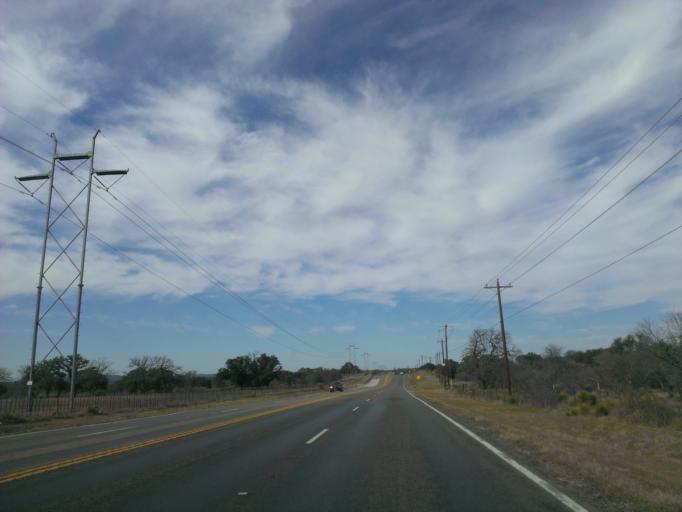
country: US
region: Texas
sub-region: Burnet County
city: Granite Shoals
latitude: 30.6132
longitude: -98.3843
